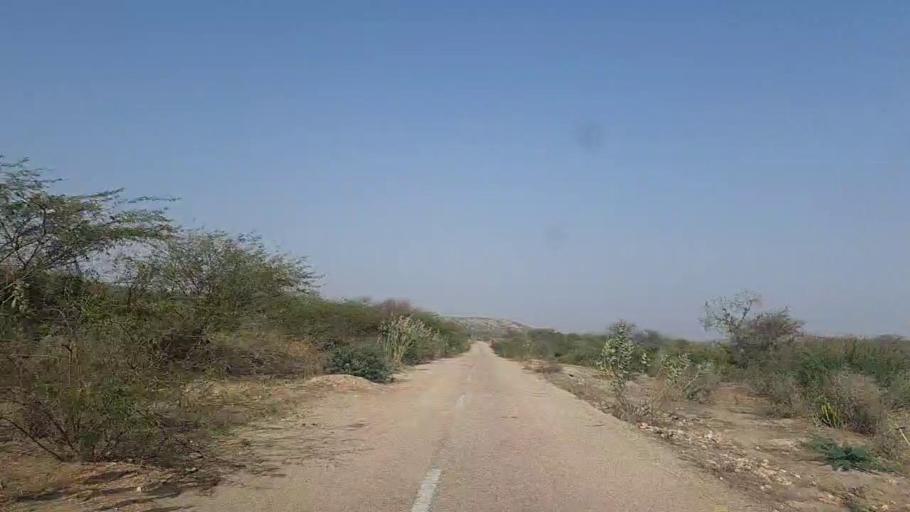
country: PK
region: Sindh
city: Naukot
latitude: 24.6058
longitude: 69.3336
